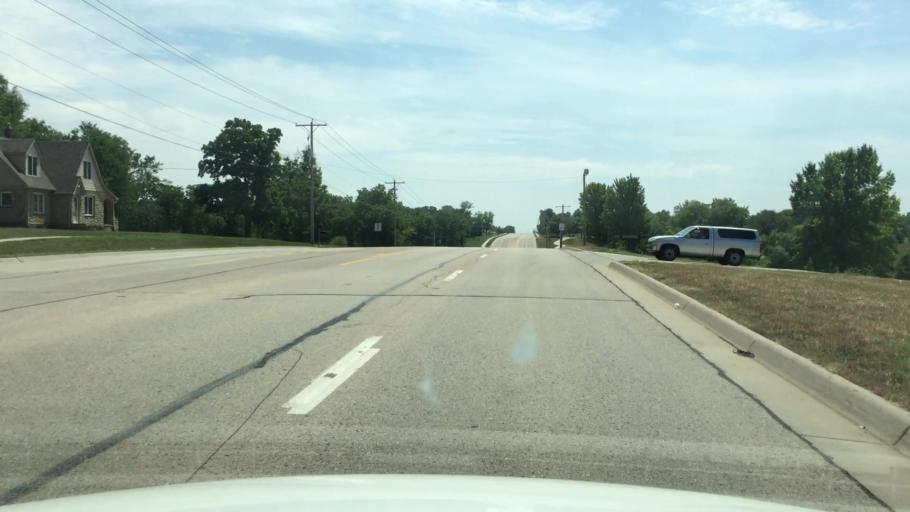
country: US
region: Kansas
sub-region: Shawnee County
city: Topeka
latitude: 39.0105
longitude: -95.6144
